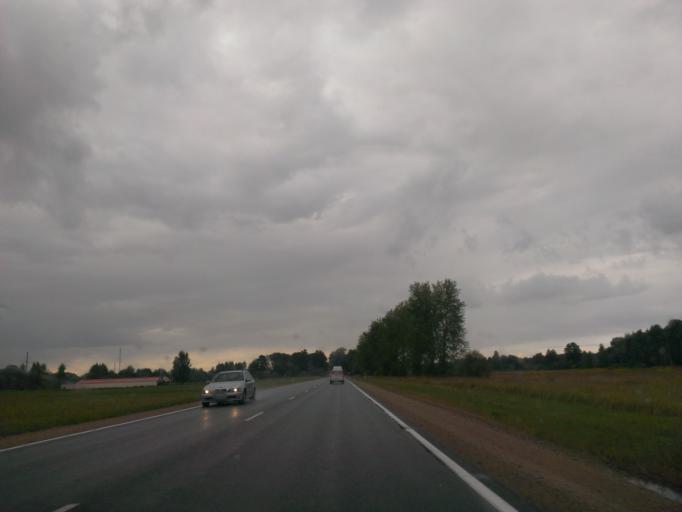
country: LV
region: Kegums
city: Kegums
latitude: 56.7668
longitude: 24.6797
